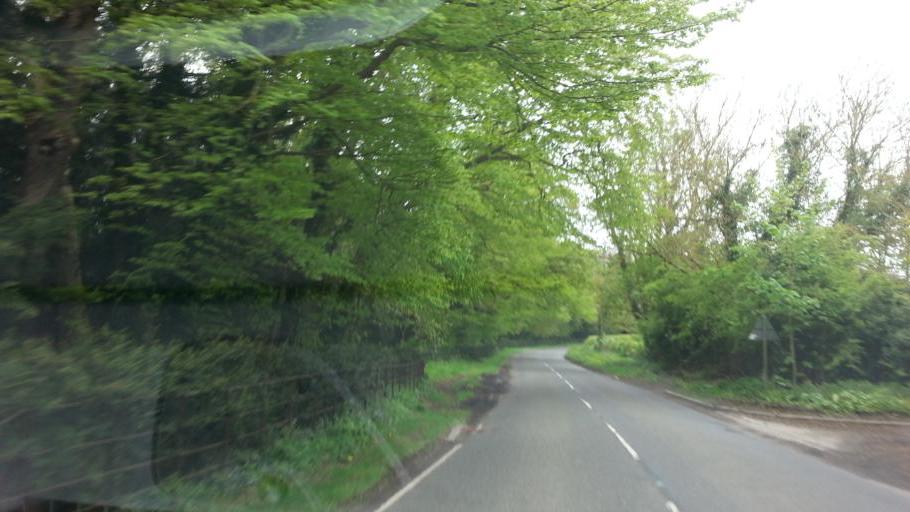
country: GB
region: England
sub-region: Lincolnshire
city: Grantham
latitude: 52.8649
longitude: -0.5554
